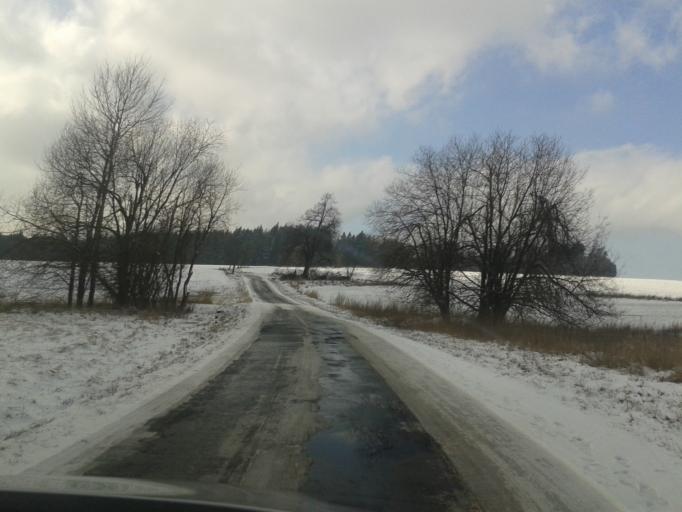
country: CZ
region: Olomoucky
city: Horni Stepanov
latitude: 49.5363
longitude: 16.8339
